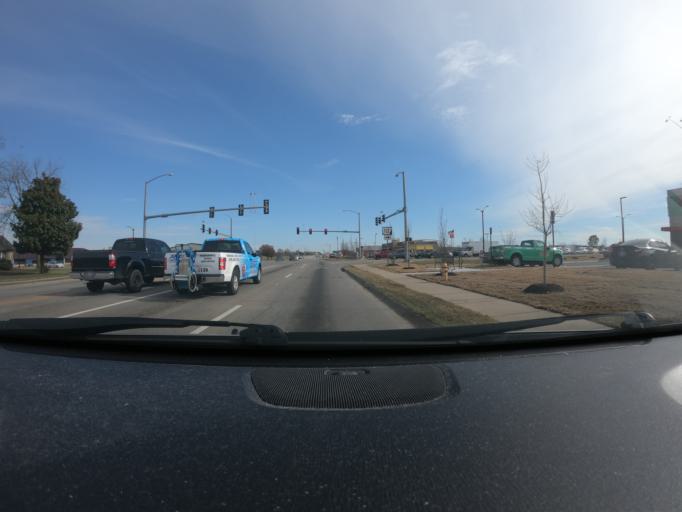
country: US
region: Arkansas
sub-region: Benton County
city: Bentonville
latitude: 36.3356
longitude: -94.2233
